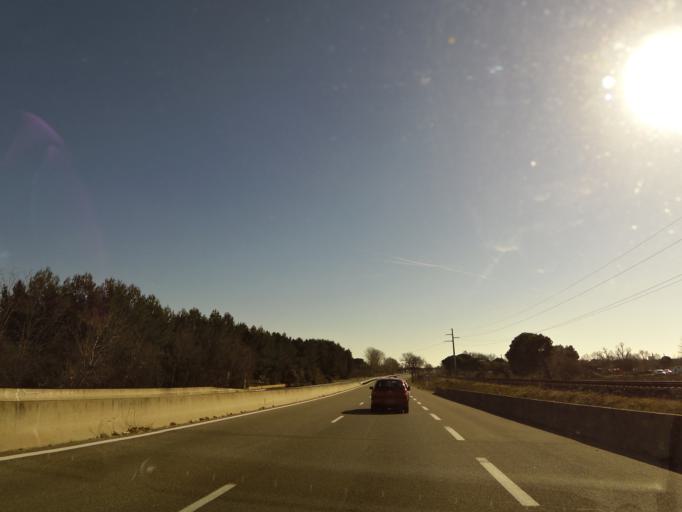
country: FR
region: Languedoc-Roussillon
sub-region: Departement du Gard
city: Aigues-Mortes
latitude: 43.5860
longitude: 4.1965
